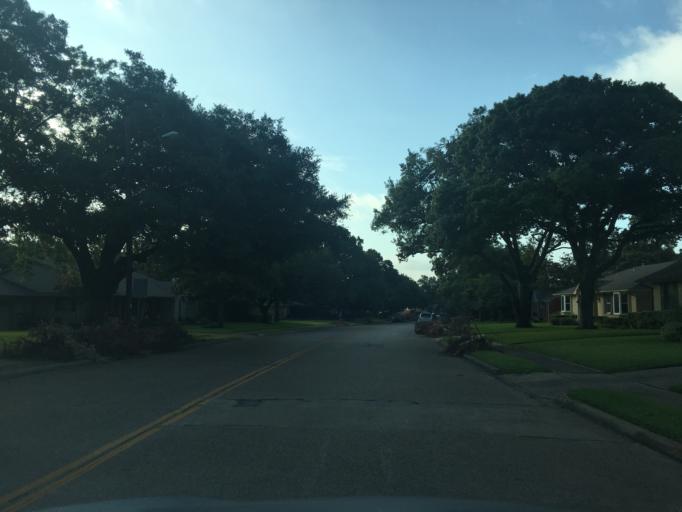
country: US
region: Texas
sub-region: Dallas County
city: Highland Park
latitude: 32.8466
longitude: -96.7555
